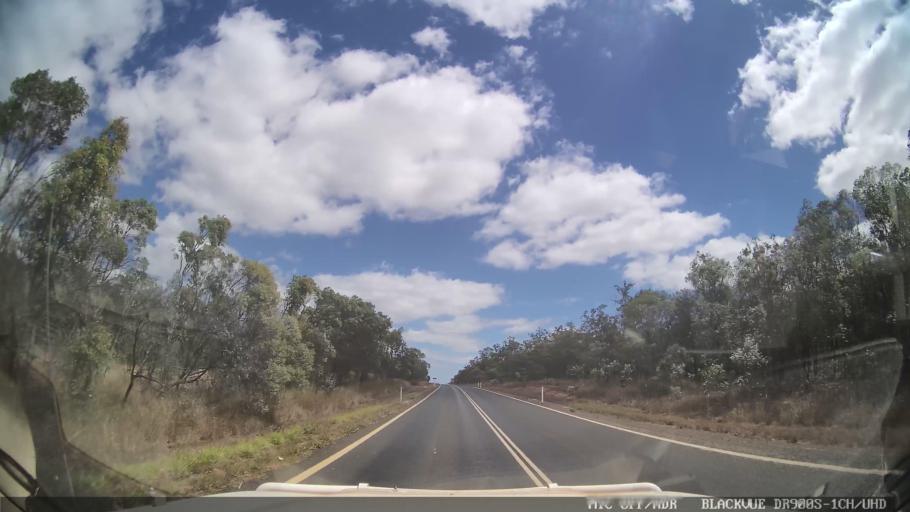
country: AU
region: Queensland
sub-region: Tablelands
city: Ravenshoe
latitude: -17.9081
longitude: 144.8825
